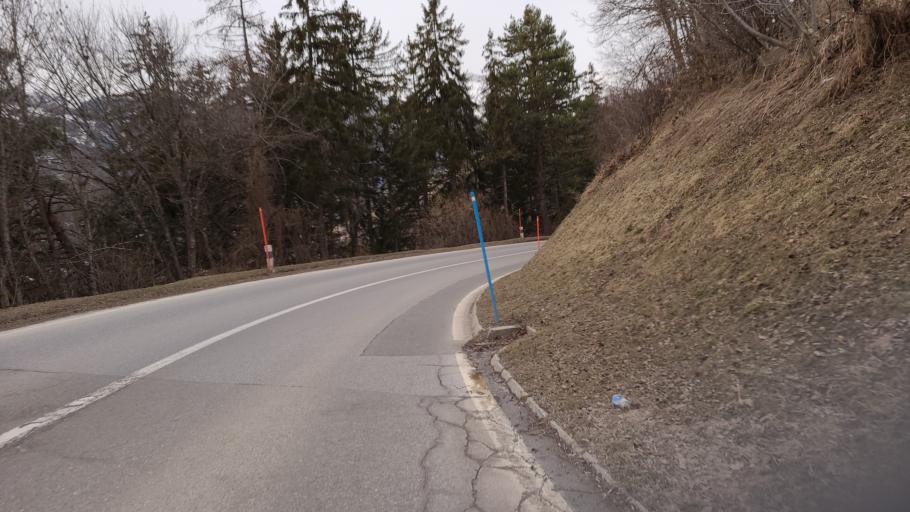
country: CH
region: Valais
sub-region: Sierre District
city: Lens
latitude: 46.2821
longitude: 7.4425
